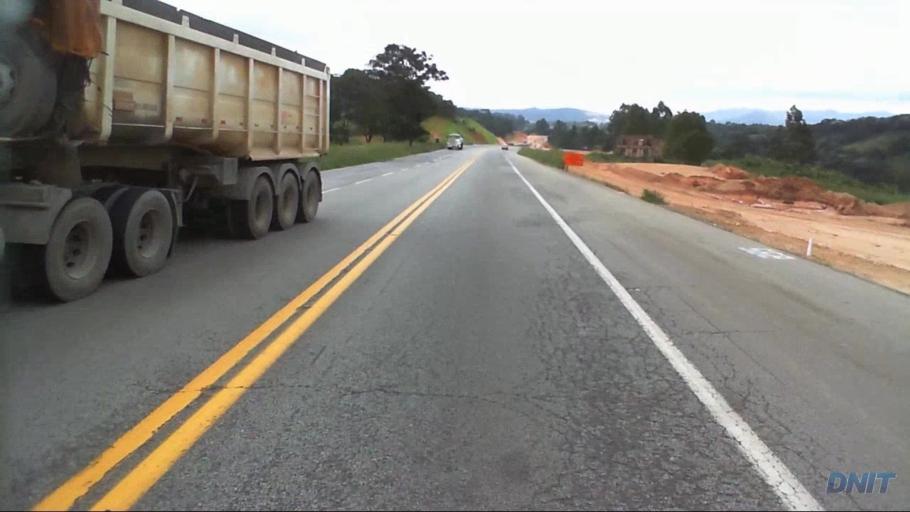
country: BR
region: Minas Gerais
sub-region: Caete
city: Caete
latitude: -19.7513
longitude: -43.5415
